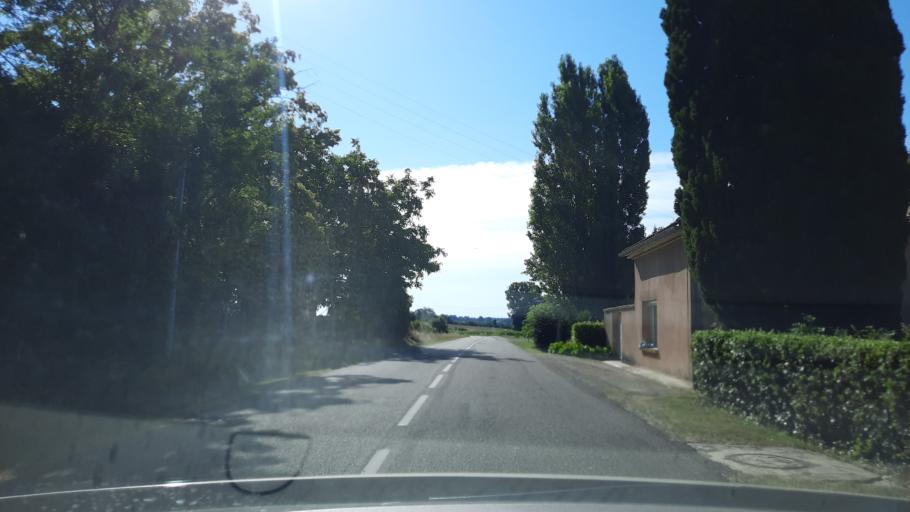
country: FR
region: Midi-Pyrenees
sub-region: Departement du Tarn-et-Garonne
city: Molieres
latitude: 44.2000
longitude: 1.3869
